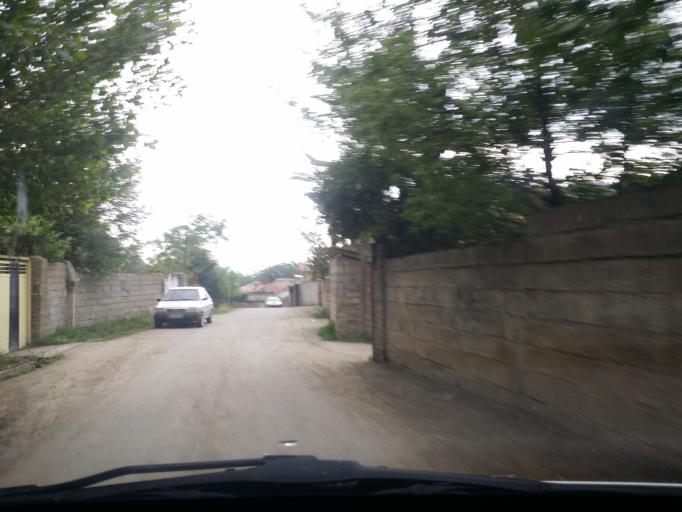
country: IR
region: Mazandaran
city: `Abbasabad
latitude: 36.5037
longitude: 51.1466
